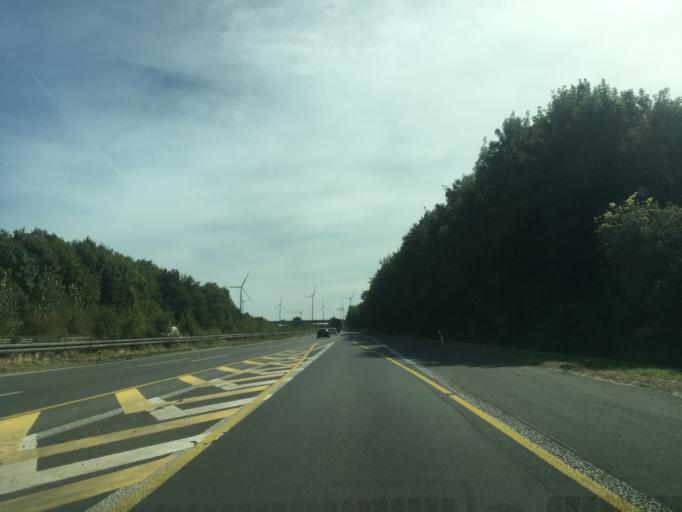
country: DE
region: North Rhine-Westphalia
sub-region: Regierungsbezirk Koln
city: Titz
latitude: 51.0362
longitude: 6.4615
